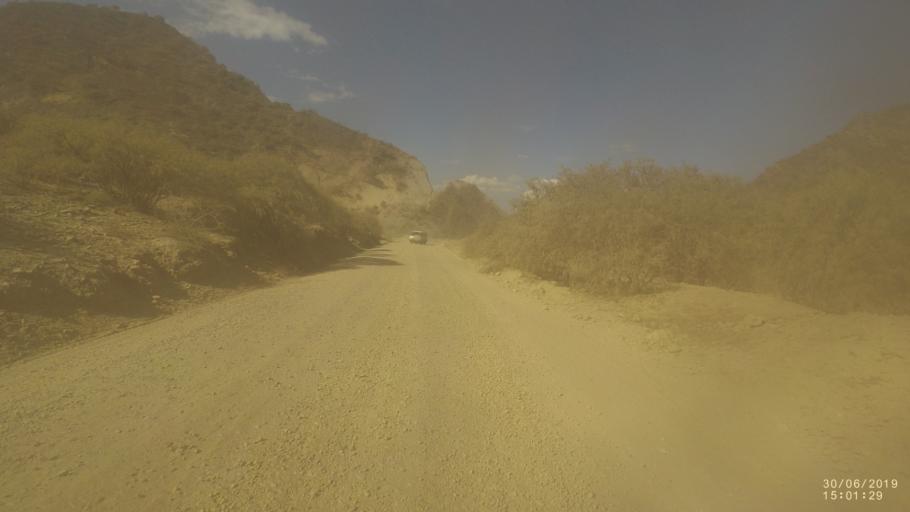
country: BO
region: Cochabamba
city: Irpa Irpa
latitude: -17.7332
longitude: -66.3359
